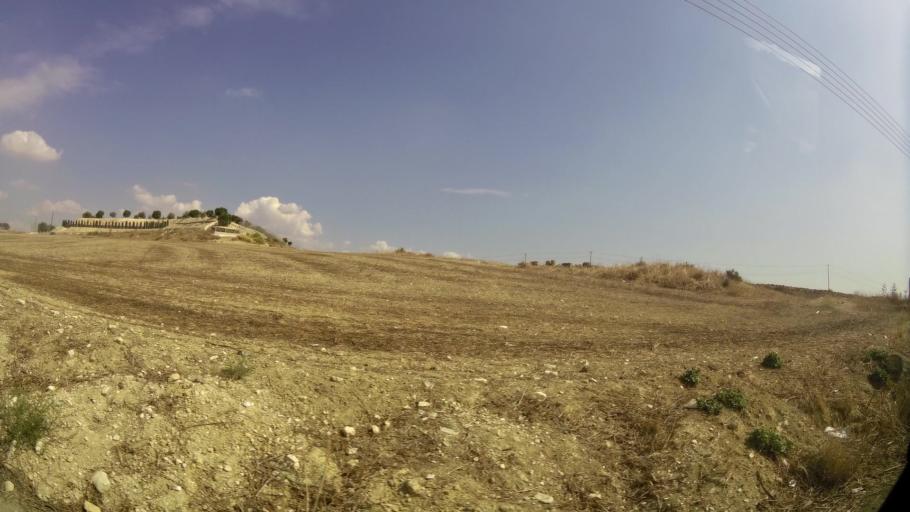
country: CY
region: Larnaka
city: Aradippou
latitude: 34.9587
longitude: 33.5738
